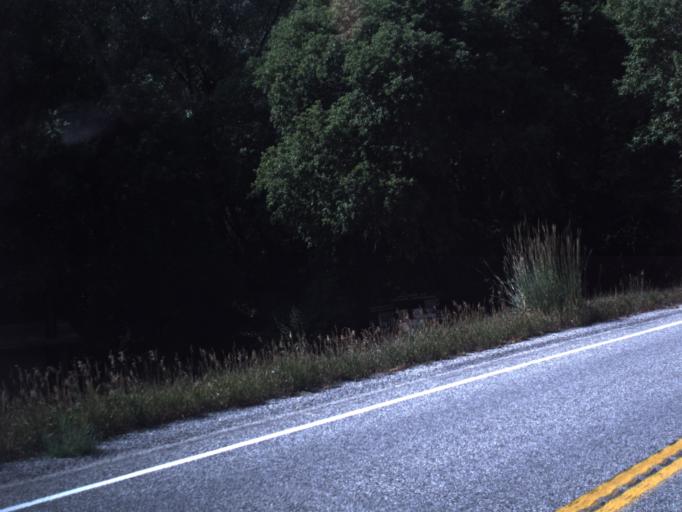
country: US
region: Utah
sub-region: Cache County
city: North Logan
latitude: 41.7971
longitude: -111.6445
